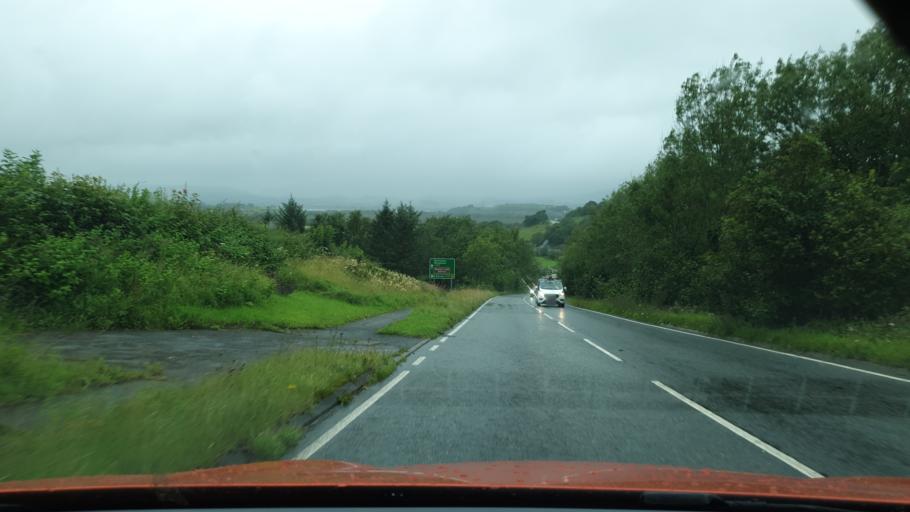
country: GB
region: England
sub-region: Cumbria
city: Askam in Furness
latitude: 54.2551
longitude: -3.1660
